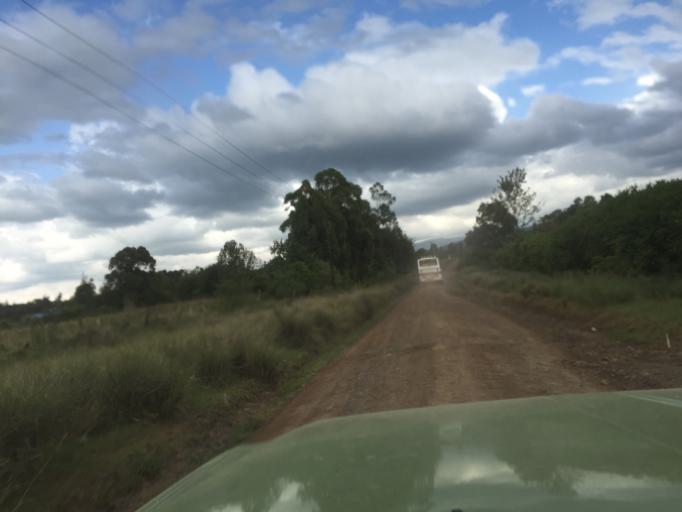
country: KE
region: Nyandarua
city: Ol Kalou
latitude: -0.4164
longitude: 36.4514
